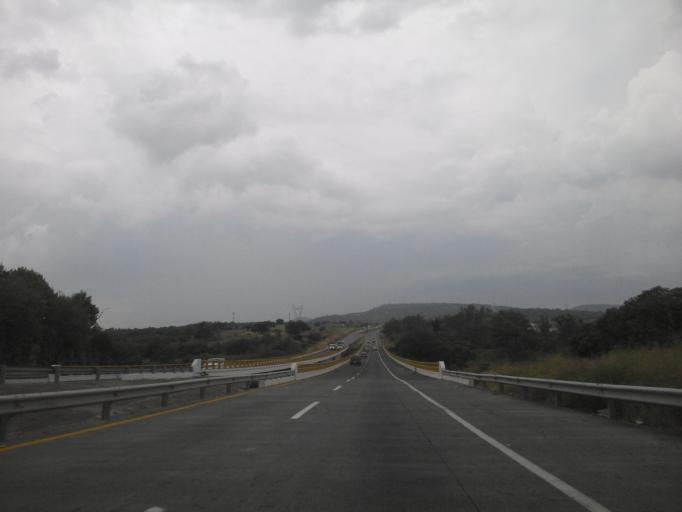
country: MX
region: Jalisco
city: Puente Grande
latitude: 20.5743
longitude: -103.1384
